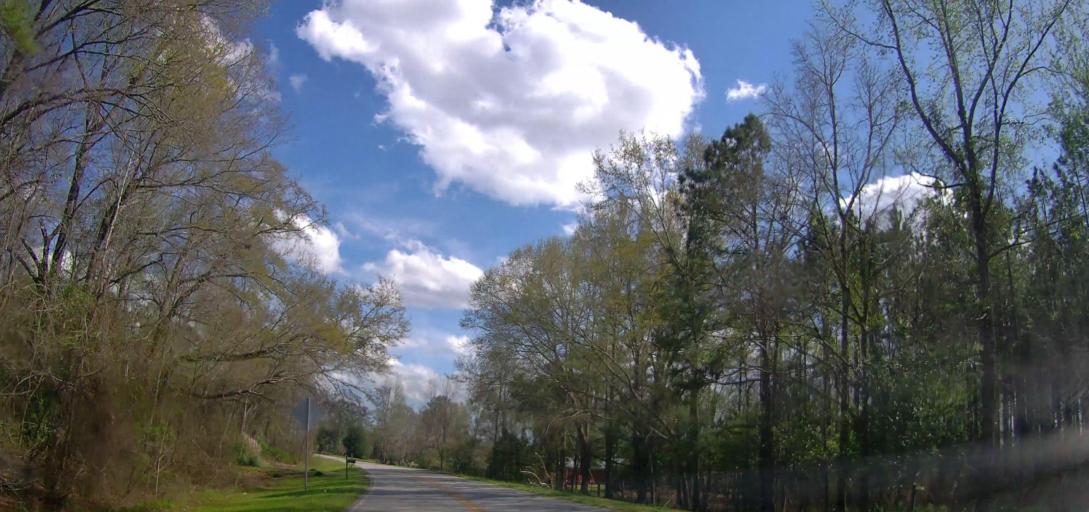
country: US
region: Georgia
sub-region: Wilkinson County
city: Gordon
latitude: 32.8468
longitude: -83.4474
